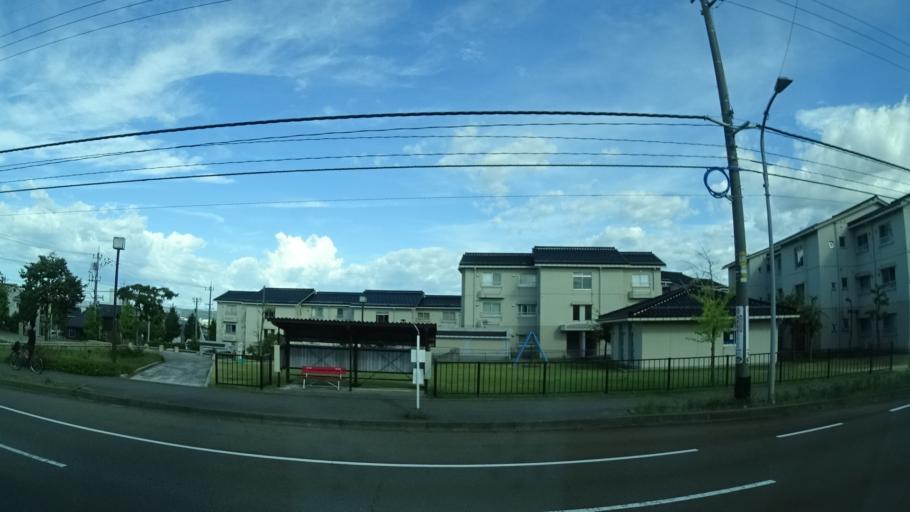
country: JP
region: Ishikawa
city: Kanazawa-shi
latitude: 36.6415
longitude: 136.6381
